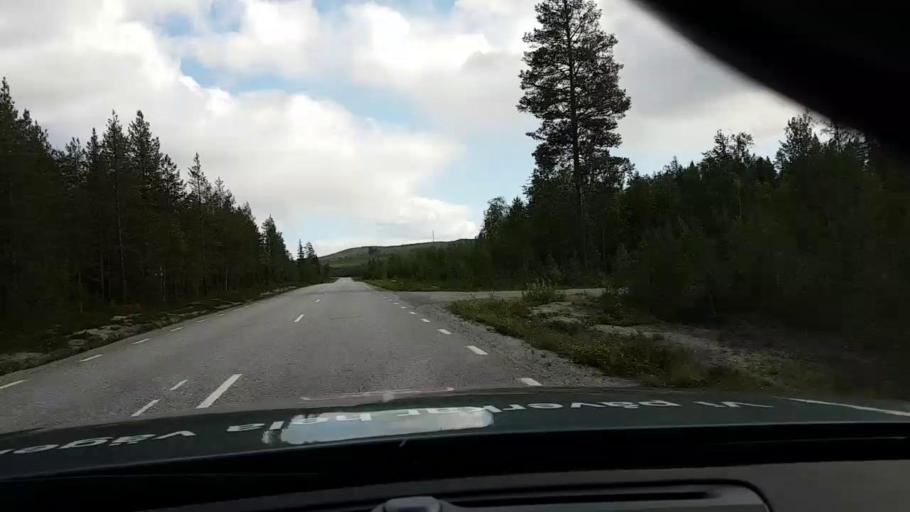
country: SE
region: Vaesternorrland
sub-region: OErnskoeldsviks Kommun
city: Bredbyn
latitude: 63.6837
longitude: 17.7788
